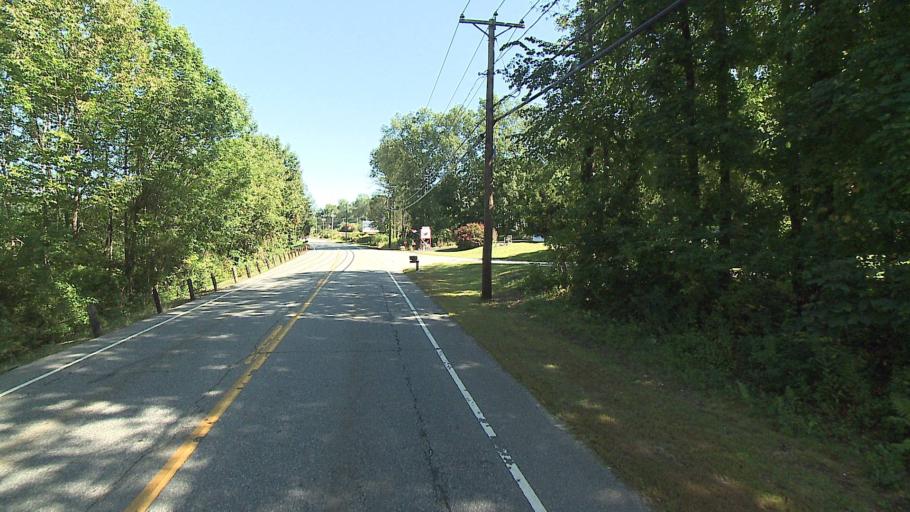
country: US
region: Connecticut
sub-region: Windham County
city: Plainfield
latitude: 41.7014
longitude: -71.9068
